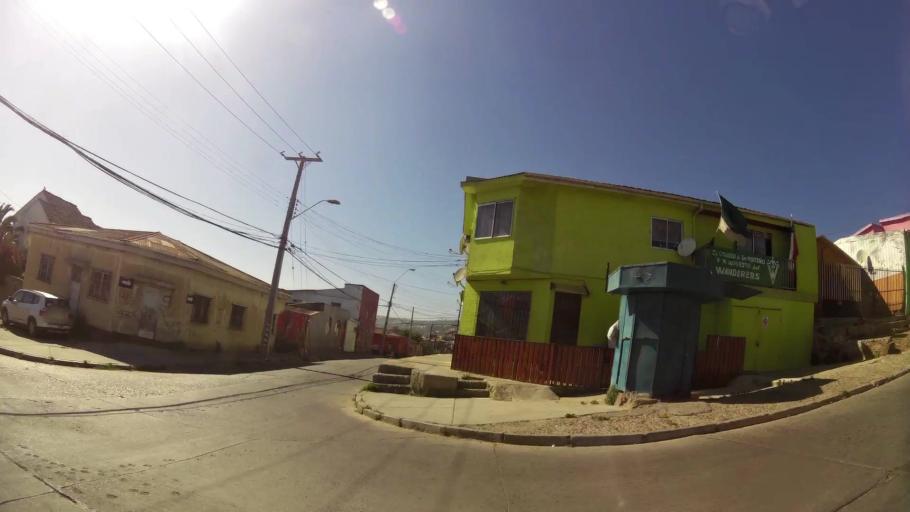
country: CL
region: Valparaiso
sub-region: Provincia de Valparaiso
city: Valparaiso
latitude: -33.0437
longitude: -71.6375
